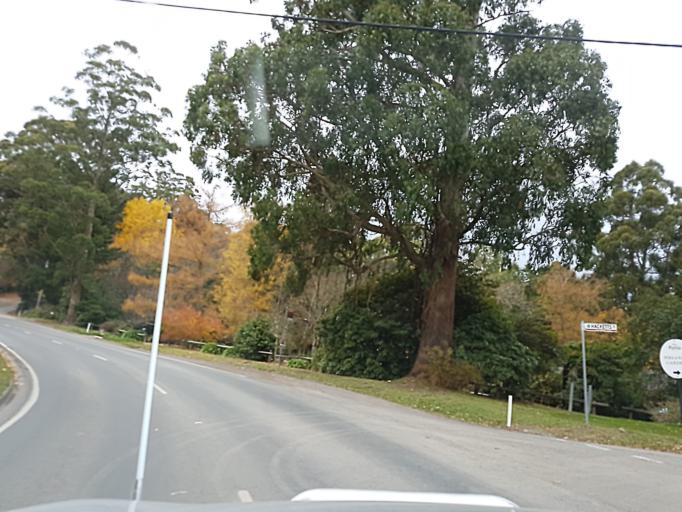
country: AU
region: Victoria
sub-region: Yarra Ranges
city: Kallista
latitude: -37.8726
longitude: 145.3808
